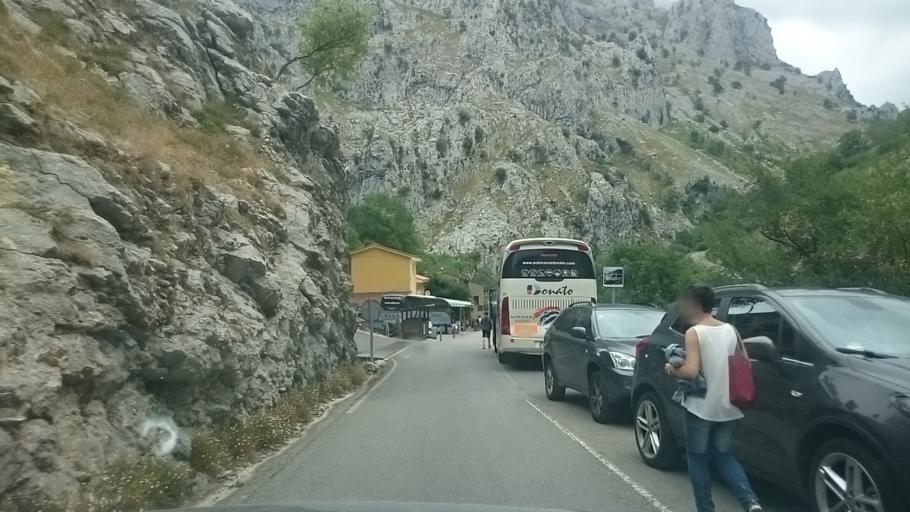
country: ES
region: Asturias
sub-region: Province of Asturias
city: Carrena
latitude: 43.2567
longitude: -4.8332
